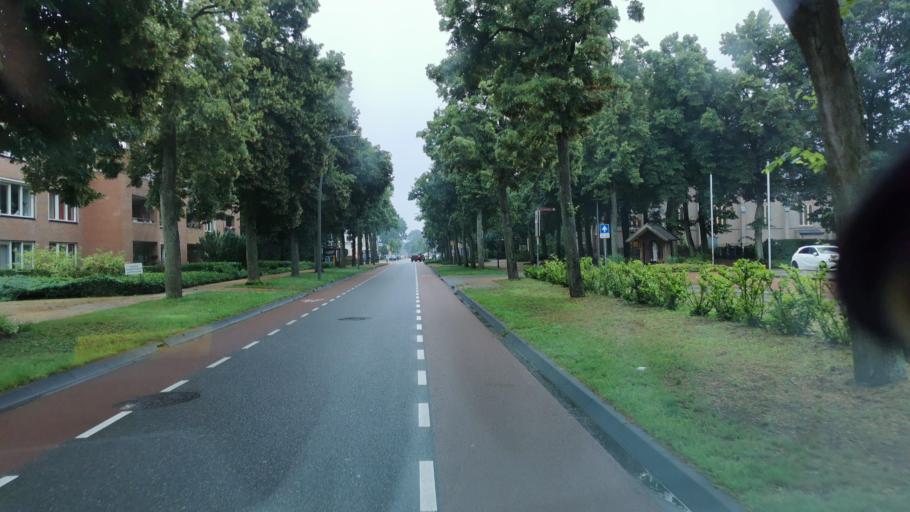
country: DE
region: North Rhine-Westphalia
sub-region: Regierungsbezirk Munster
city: Gronau
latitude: 52.2413
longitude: 7.0317
